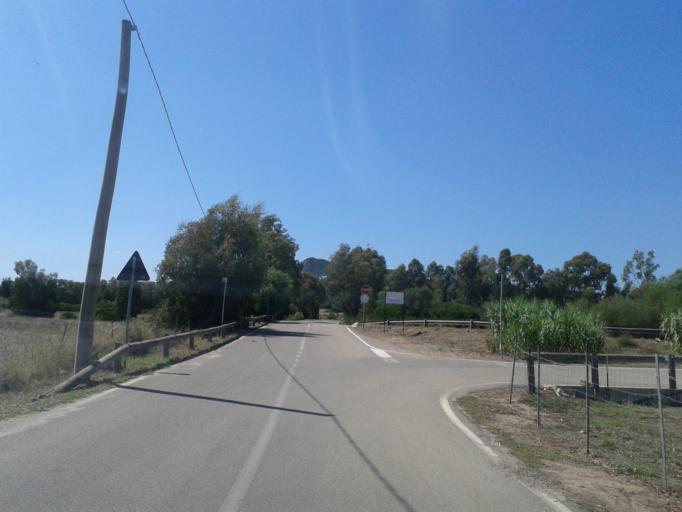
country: IT
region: Sardinia
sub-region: Provincia di Cagliari
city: Olia Speciosa
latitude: 39.2752
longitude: 9.5806
